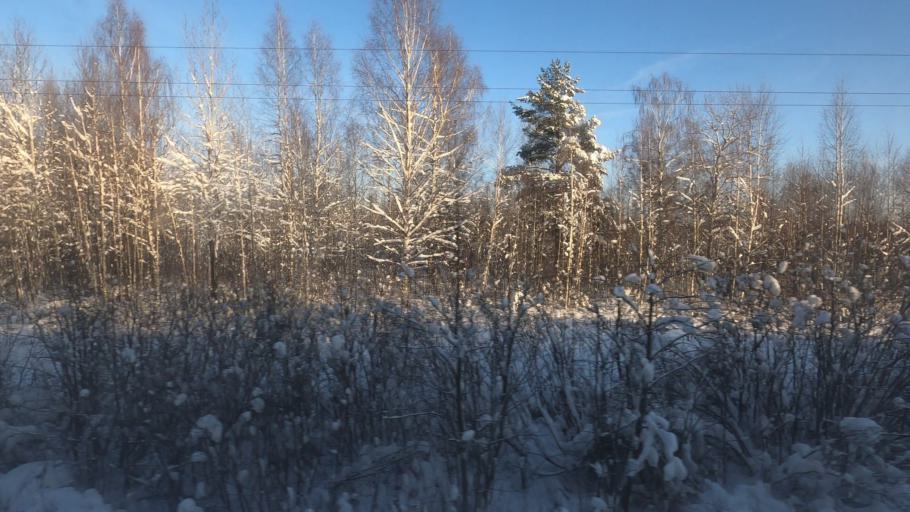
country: RU
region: Moskovskaya
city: Taldom
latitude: 56.7070
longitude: 37.5440
